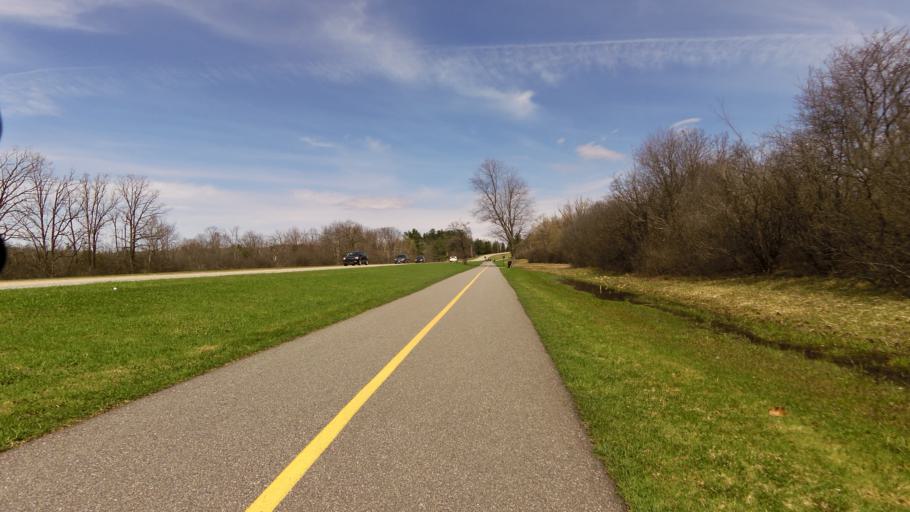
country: CA
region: Ontario
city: Ottawa
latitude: 45.4357
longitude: -75.7471
